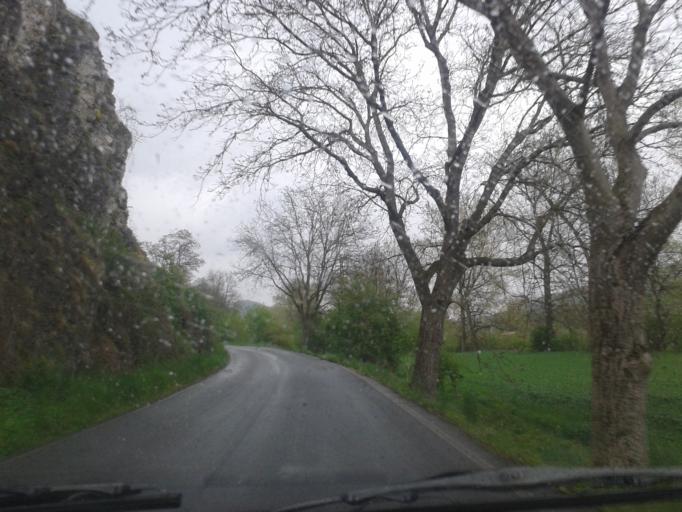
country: CZ
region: Central Bohemia
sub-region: Okres Beroun
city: Lodenice
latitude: 49.9321
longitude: 14.1574
